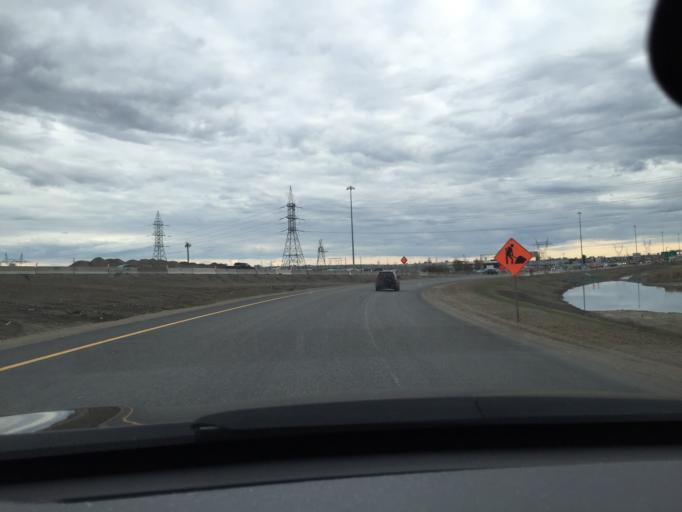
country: CA
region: Quebec
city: Quebec
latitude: 46.8370
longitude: -71.2667
